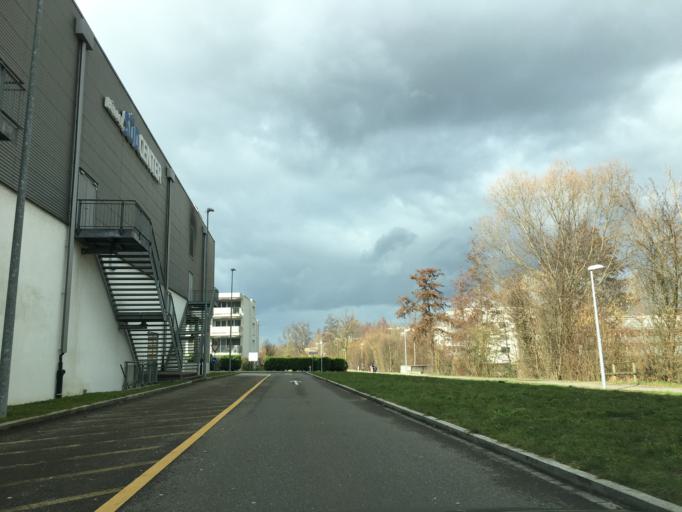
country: CH
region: Zurich
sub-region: Bezirk Buelach
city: Bachenbulach
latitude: 47.5104
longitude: 8.5414
